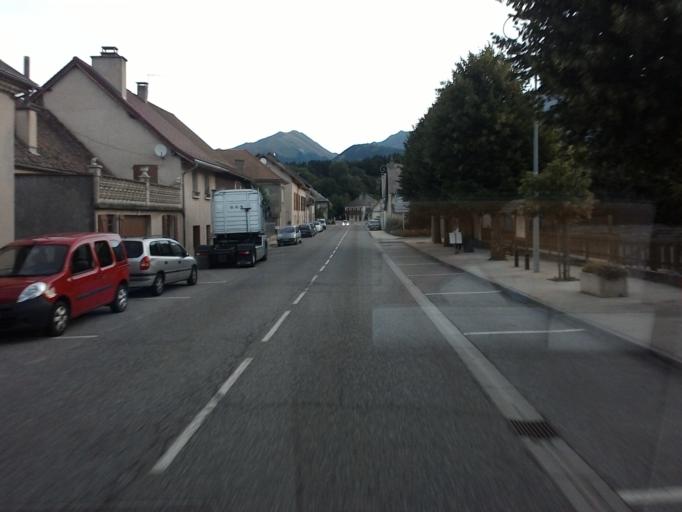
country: FR
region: Provence-Alpes-Cote d'Azur
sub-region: Departement des Hautes-Alpes
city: Saint-Bonnet-en-Champsaur
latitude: 44.7532
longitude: 6.0088
